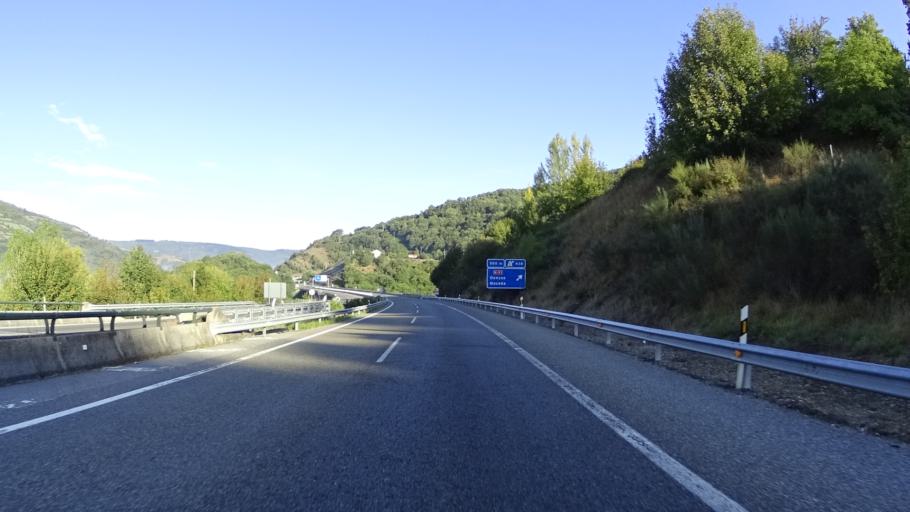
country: ES
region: Galicia
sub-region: Provincia de Lugo
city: San Roman
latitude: 42.7596
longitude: -7.0760
